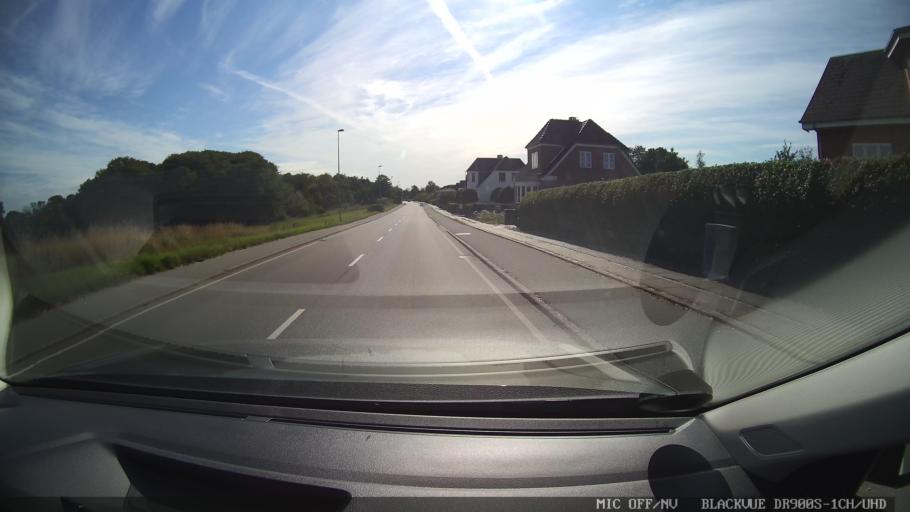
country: DK
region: North Denmark
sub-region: Mariagerfjord Kommune
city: Arden
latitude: 56.7659
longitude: 9.8663
